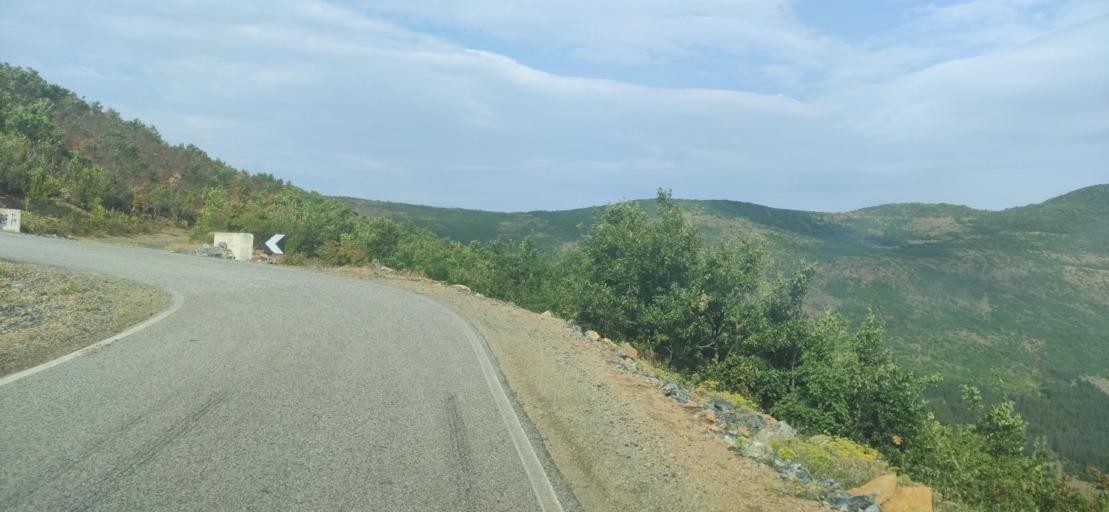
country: AL
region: Shkoder
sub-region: Rrethi i Pukes
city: Iballe
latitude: 42.1731
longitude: 19.9928
